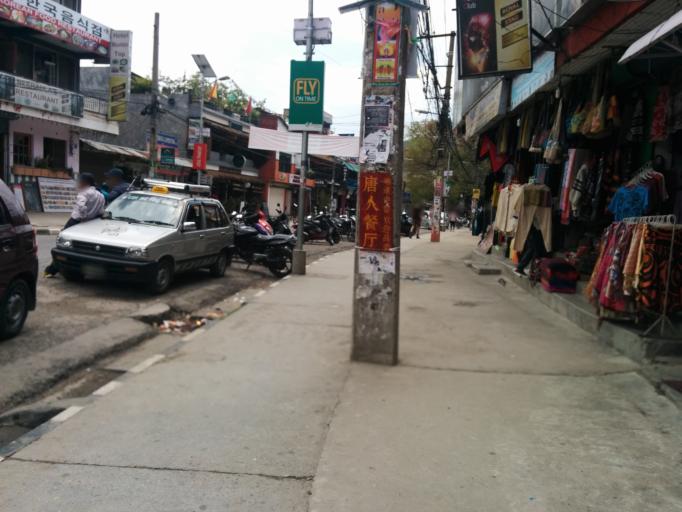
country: NP
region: Western Region
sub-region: Gandaki Zone
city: Pokhara
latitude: 28.2118
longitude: 83.9571
